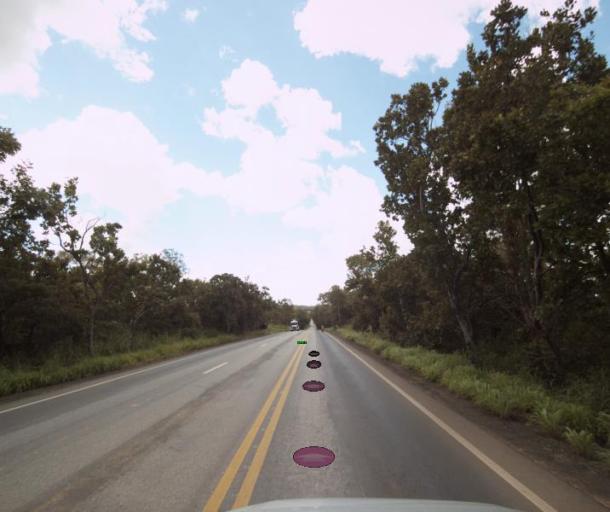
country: BR
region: Goias
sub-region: Porangatu
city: Porangatu
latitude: -13.7716
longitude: -49.0304
